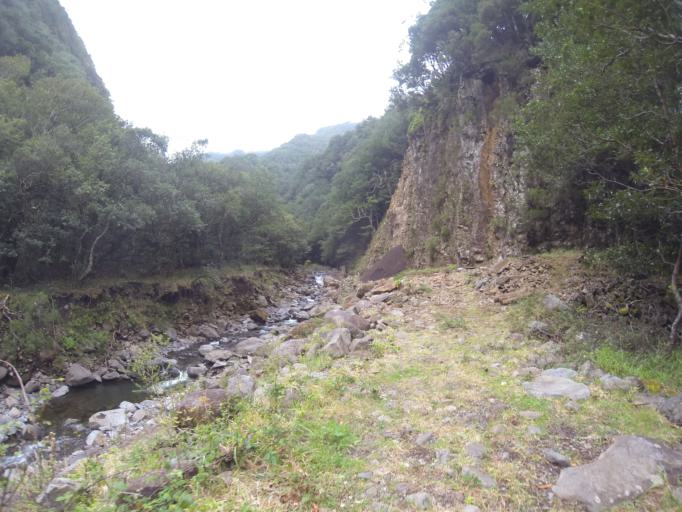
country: PT
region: Madeira
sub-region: Sao Vicente
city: Sao Vicente
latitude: 32.7926
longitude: -17.1135
